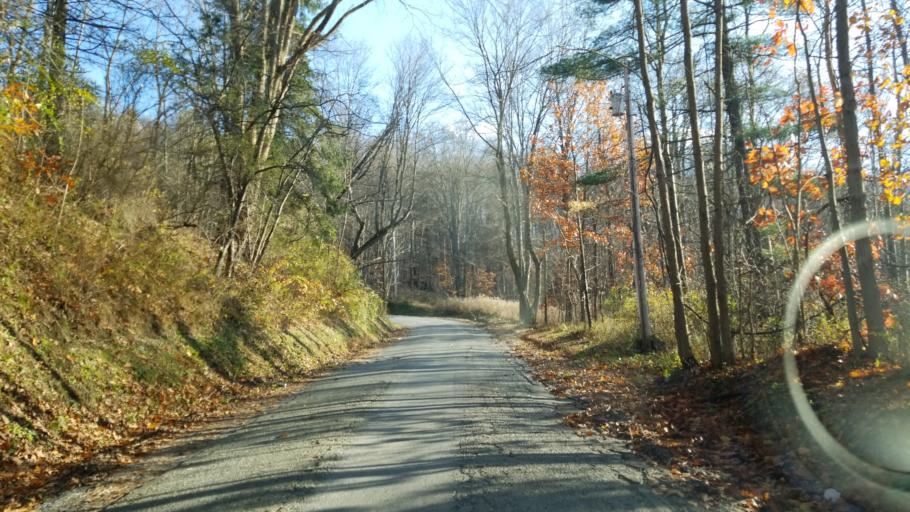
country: US
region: Pennsylvania
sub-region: Clearfield County
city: Treasure Lake
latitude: 41.1524
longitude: -78.6651
